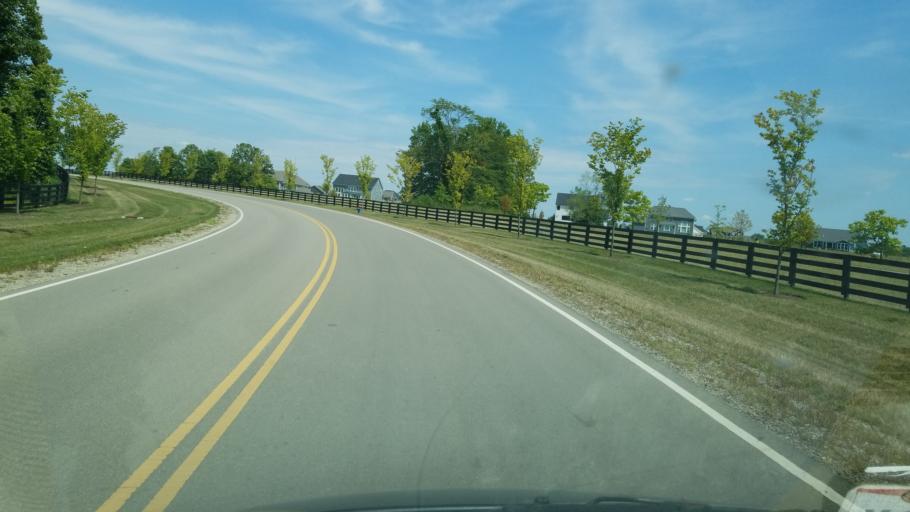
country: US
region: Ohio
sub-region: Union County
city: New California
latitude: 40.1838
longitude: -83.1878
